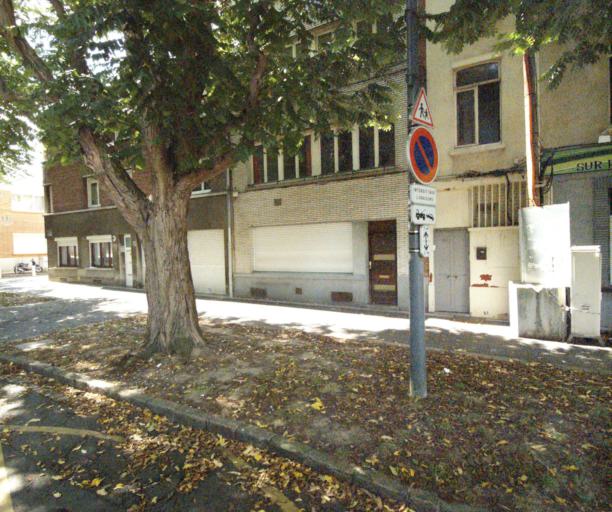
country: FR
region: Nord-Pas-de-Calais
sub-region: Departement du Nord
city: La Madeleine
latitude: 50.6259
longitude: 3.0907
